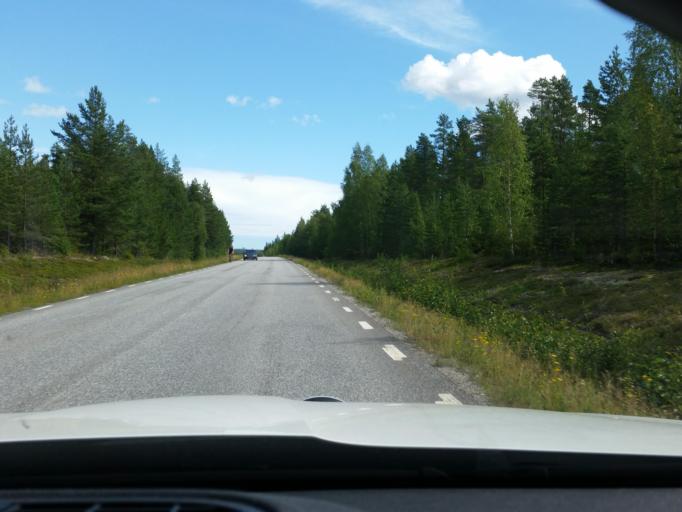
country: SE
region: Norrbotten
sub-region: Pitea Kommun
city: Hortlax
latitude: 65.2694
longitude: 21.3399
